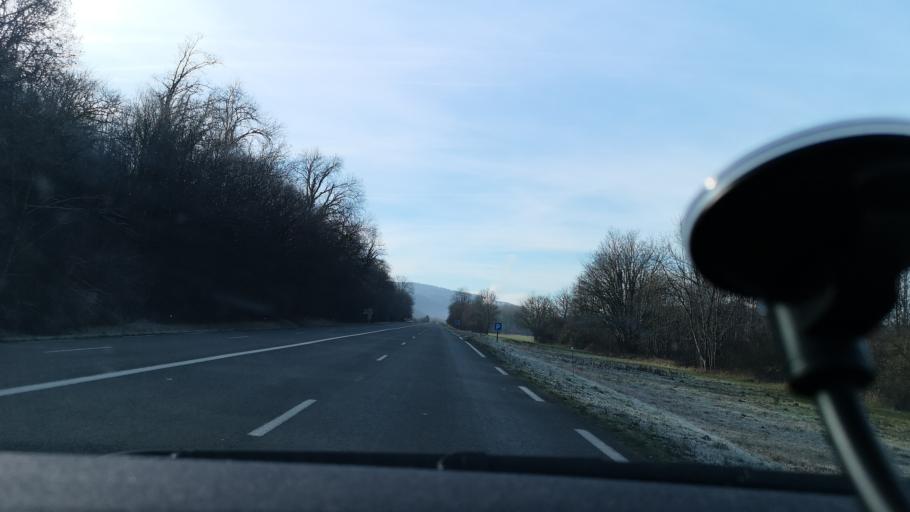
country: FR
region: Franche-Comte
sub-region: Departement du Doubs
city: Novillars
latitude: 47.2937
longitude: 6.1529
